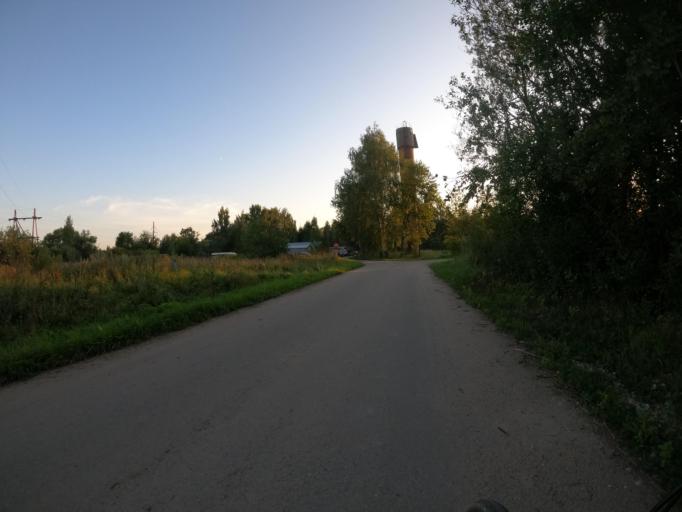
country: RU
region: Moskovskaya
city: Malino
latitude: 55.0919
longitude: 38.2804
